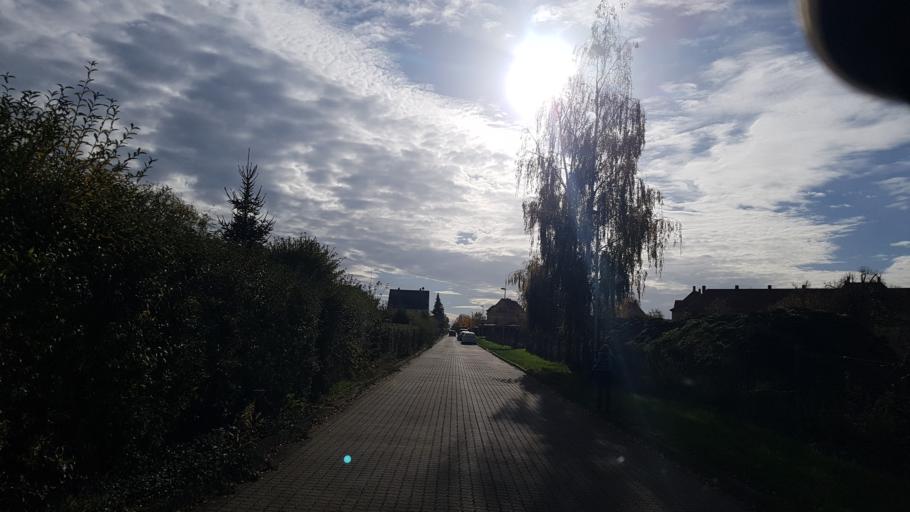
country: DE
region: Saxony
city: Oschatz
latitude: 51.2968
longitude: 13.1196
